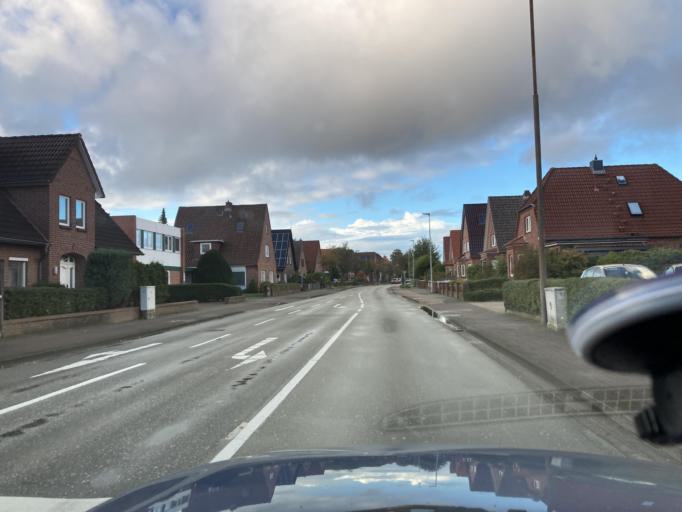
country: DE
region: Schleswig-Holstein
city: Heide
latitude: 54.1964
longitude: 9.1048
